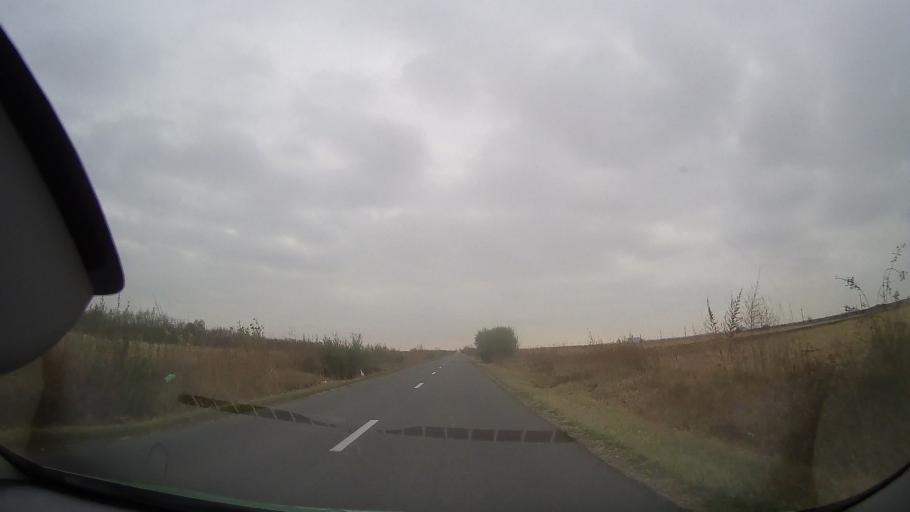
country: RO
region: Ialomita
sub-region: Comuna Manasia
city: Manasia
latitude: 44.7331
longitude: 26.7007
